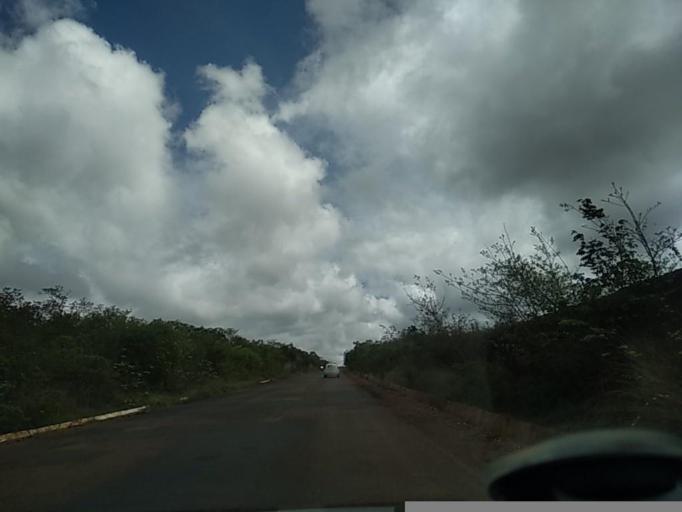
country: BR
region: Bahia
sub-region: Caetite
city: Caetite
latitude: -14.0399
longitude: -42.4863
